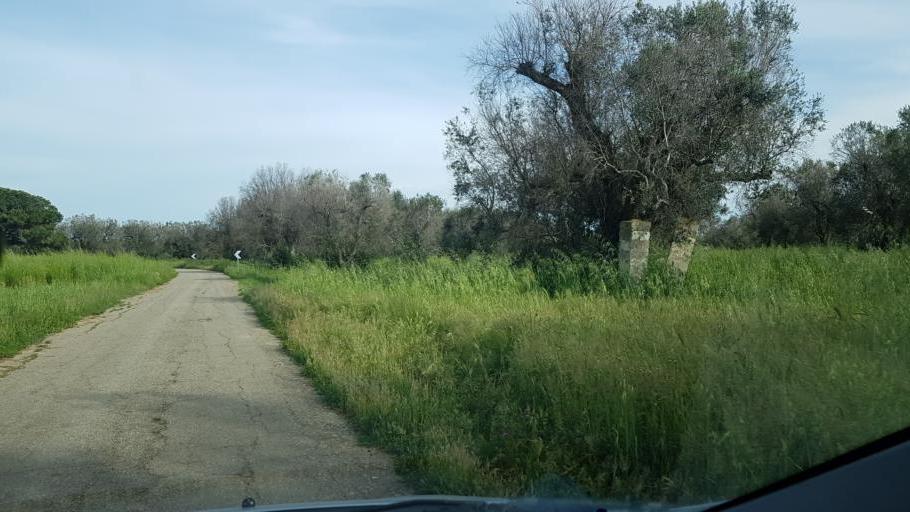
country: IT
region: Apulia
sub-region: Provincia di Brindisi
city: Tuturano
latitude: 40.5303
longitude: 17.9639
